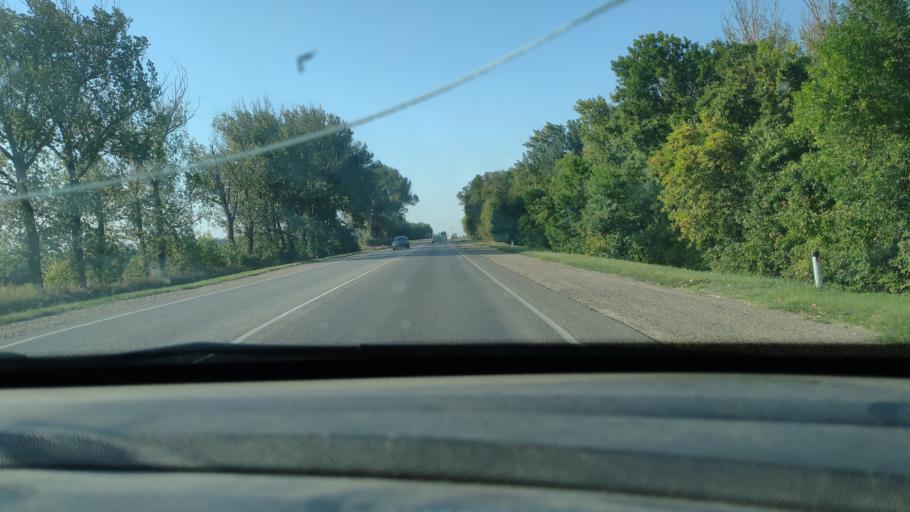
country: RU
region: Krasnodarskiy
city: Medvedovskaya
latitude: 45.4565
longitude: 38.9881
